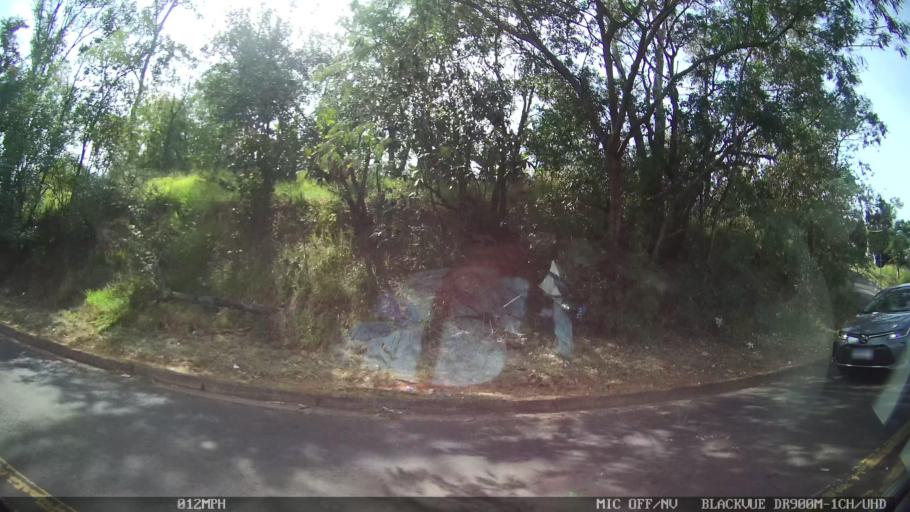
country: BR
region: Sao Paulo
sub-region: Piracicaba
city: Piracicaba
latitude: -22.7614
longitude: -47.5997
